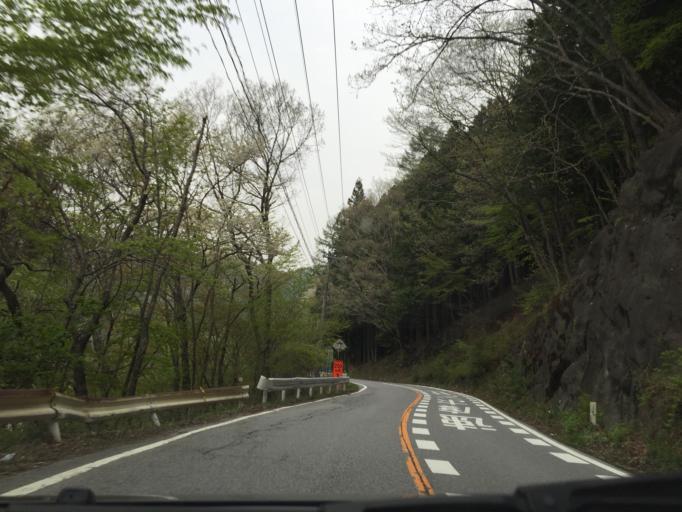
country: JP
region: Tochigi
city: Nikko
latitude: 36.9555
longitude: 139.6939
